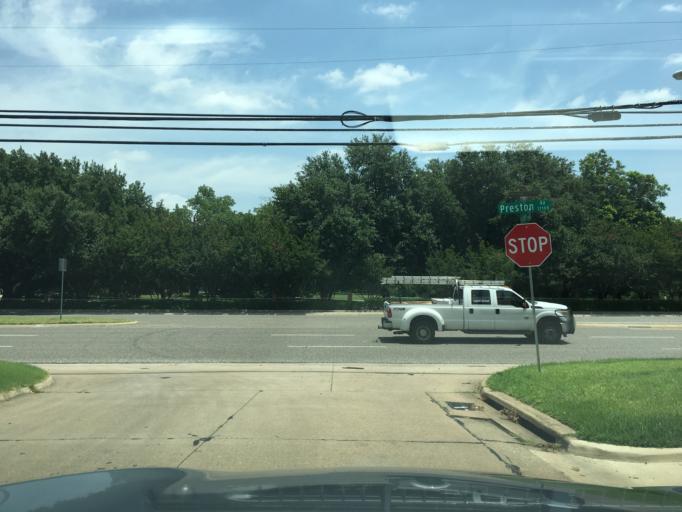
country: US
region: Texas
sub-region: Dallas County
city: Addison
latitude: 32.9143
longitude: -96.8043
